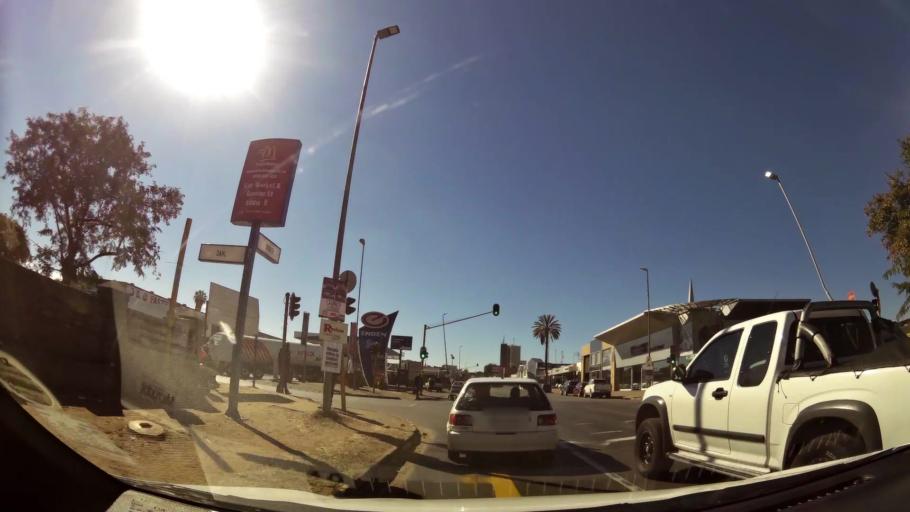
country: ZA
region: Limpopo
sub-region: Capricorn District Municipality
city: Polokwane
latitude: -23.9103
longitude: 29.4467
